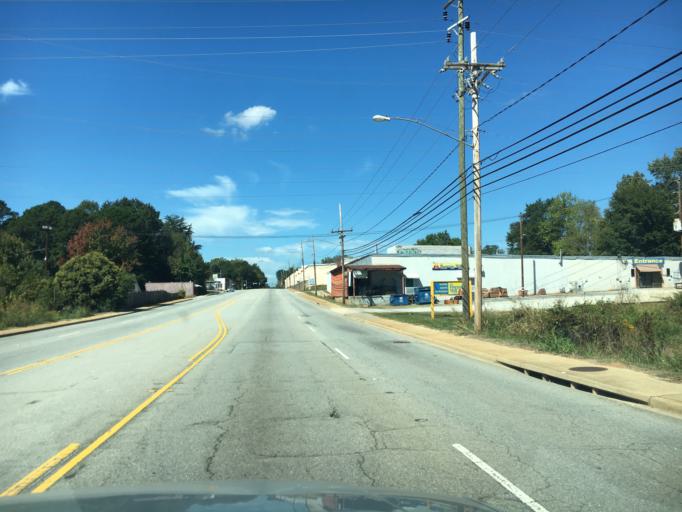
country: US
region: South Carolina
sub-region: Spartanburg County
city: Spartanburg
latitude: 34.9350
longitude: -81.9011
